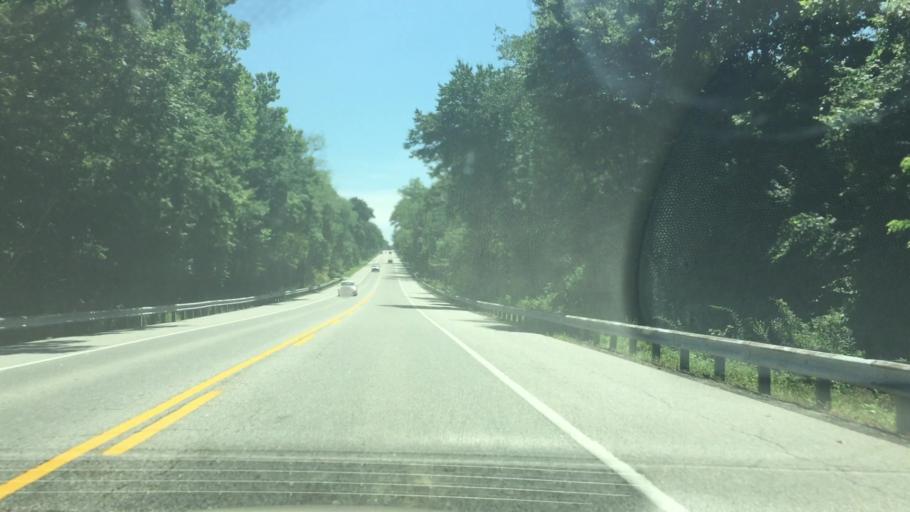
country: US
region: Maryland
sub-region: Cecil County
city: Rising Sun
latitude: 39.6523
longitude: -76.0739
